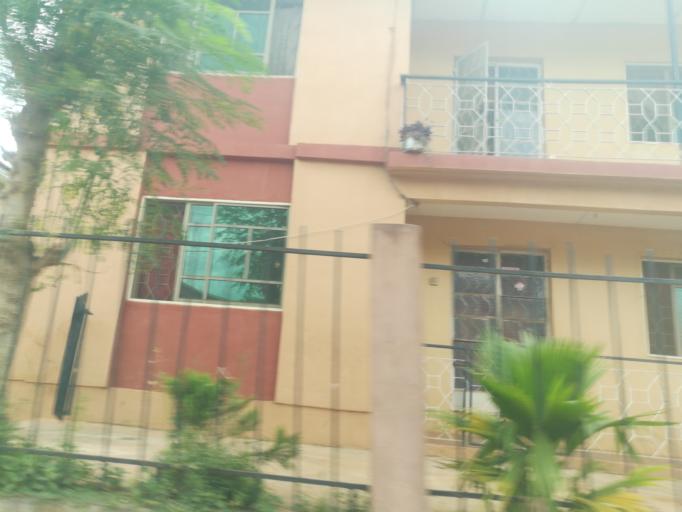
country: NG
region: Oyo
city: Ibadan
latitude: 7.4071
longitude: 3.9290
